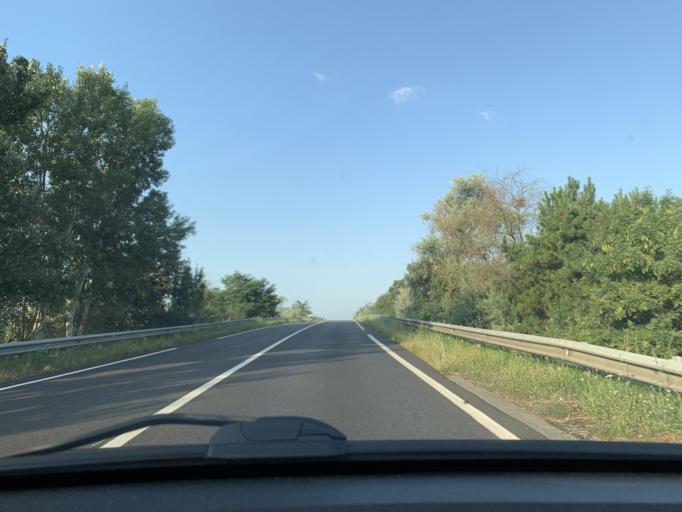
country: FR
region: Midi-Pyrenees
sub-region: Departement de la Haute-Garonne
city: Labege
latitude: 43.5362
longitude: 1.5272
